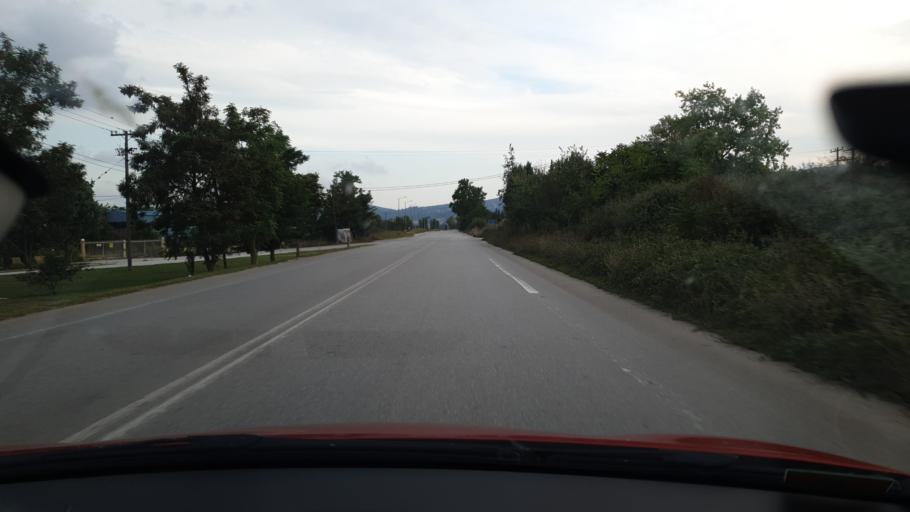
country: GR
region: Central Macedonia
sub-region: Nomos Thessalonikis
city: Liti
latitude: 40.7740
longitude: 22.9961
